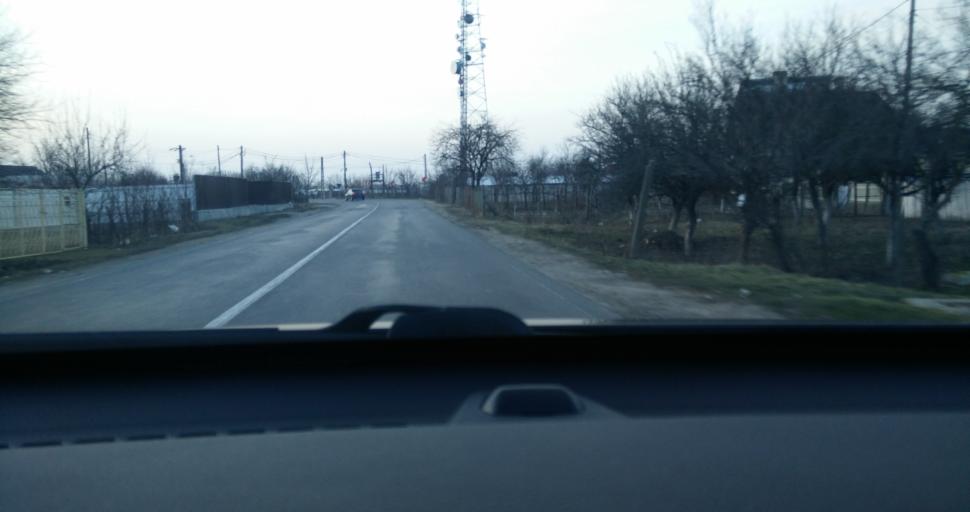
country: RO
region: Vrancea
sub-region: Comuna Milcovul
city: Milcovul
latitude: 45.6788
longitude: 27.2360
